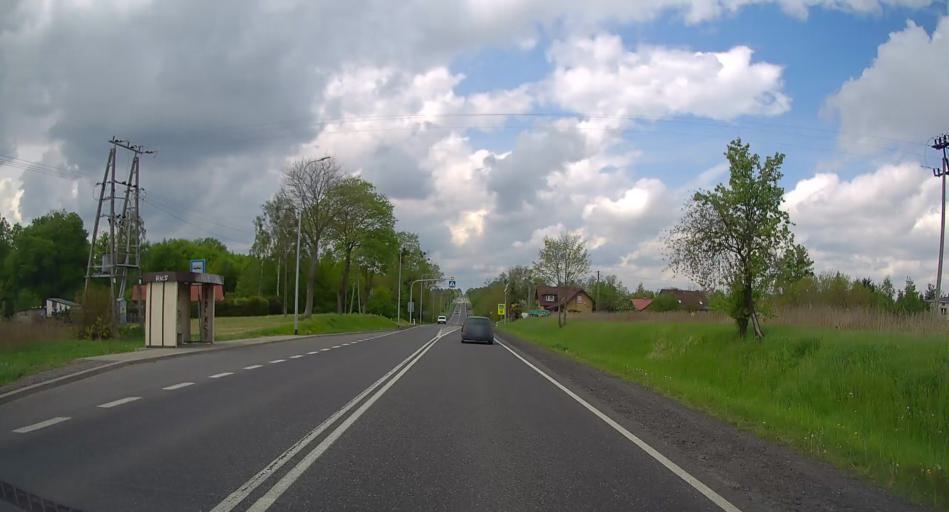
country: PL
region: Masovian Voivodeship
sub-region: Powiat nowodworski
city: Zakroczym
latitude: 52.4417
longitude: 20.5467
